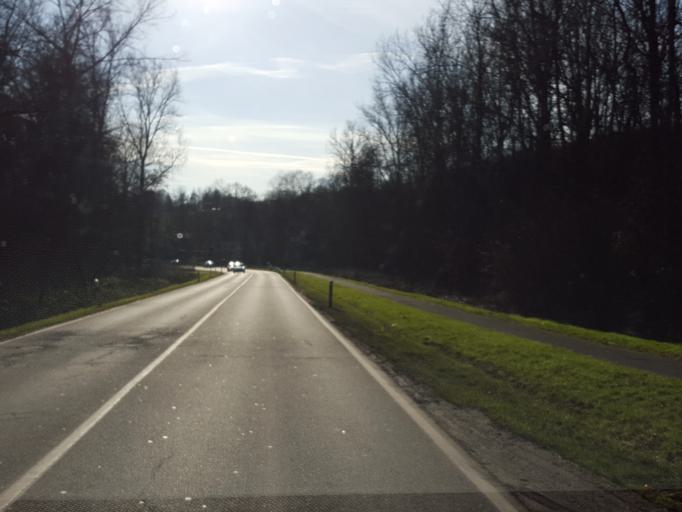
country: DE
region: Saarland
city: Puttlingen
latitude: 49.2715
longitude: 6.8756
